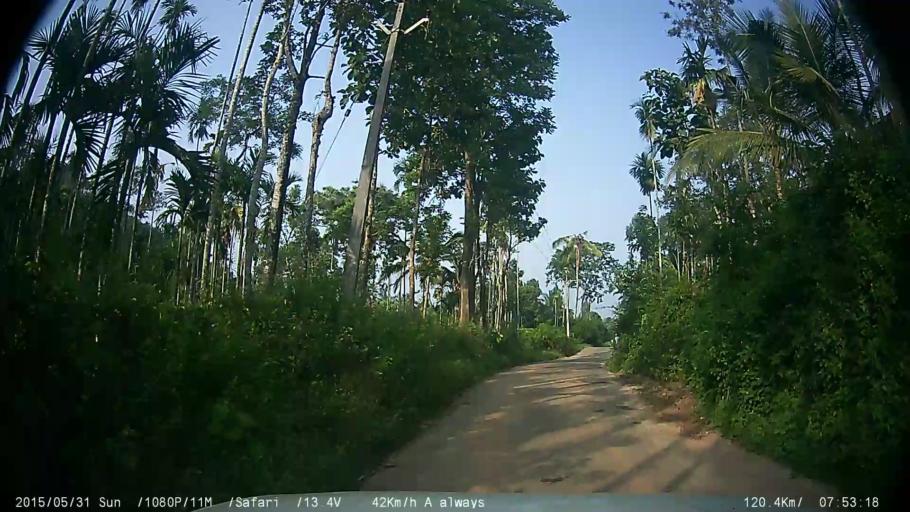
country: IN
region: Kerala
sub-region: Wayanad
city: Kalpetta
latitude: 11.6413
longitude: 76.0851
